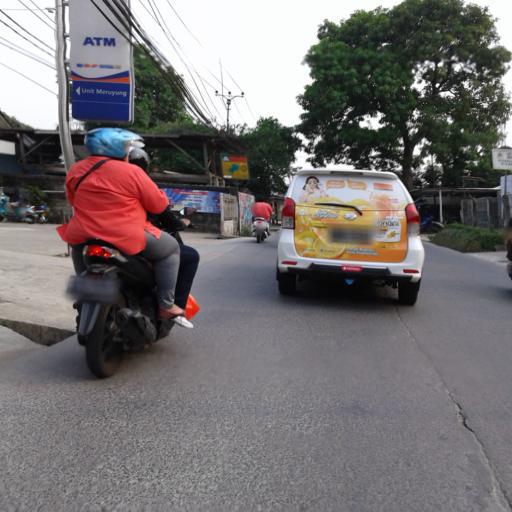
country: ID
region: West Java
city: Sawangan
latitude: -6.3803
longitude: 106.7693
